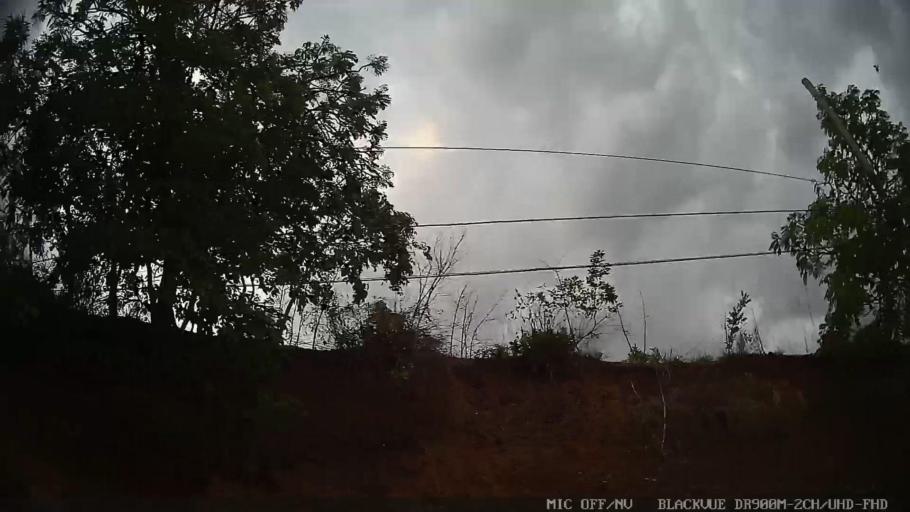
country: BR
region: Sao Paulo
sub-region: Braganca Paulista
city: Braganca Paulista
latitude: -22.9140
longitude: -46.5230
